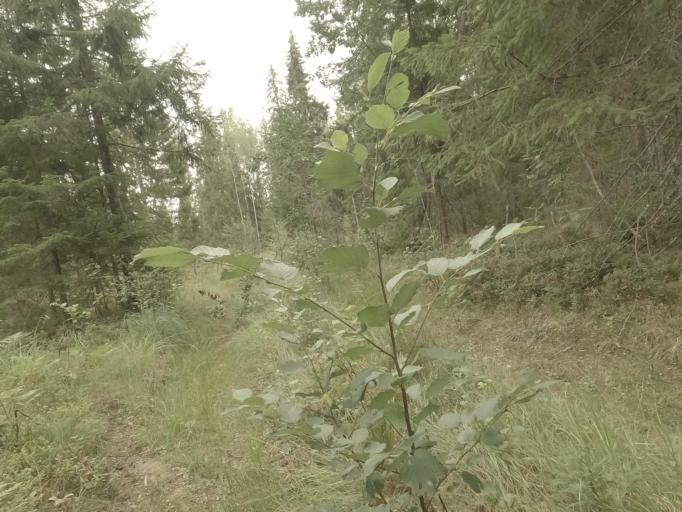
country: RU
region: Leningrad
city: Kamennogorsk
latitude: 61.0498
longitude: 29.1825
